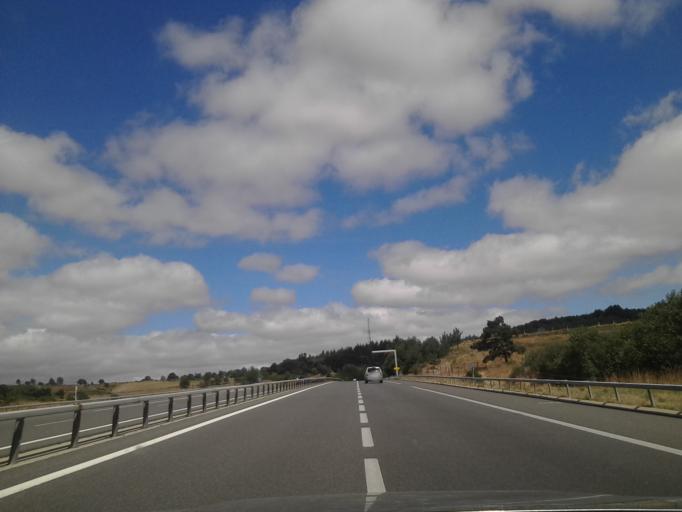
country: FR
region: Languedoc-Roussillon
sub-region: Departement de la Lozere
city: Marvejols
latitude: 44.6286
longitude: 3.2440
